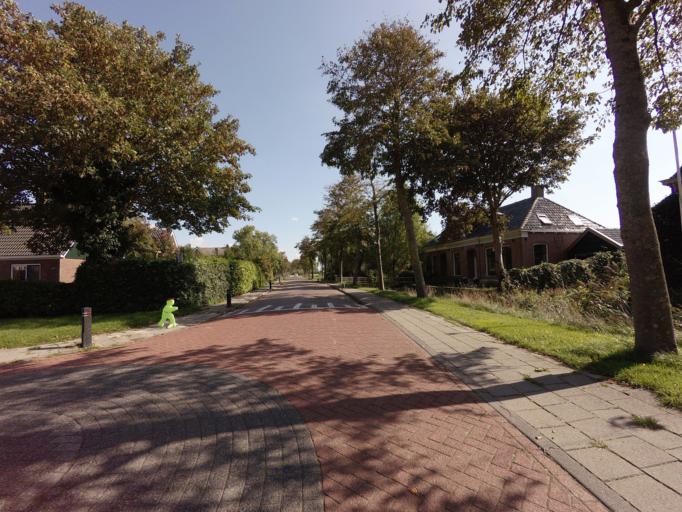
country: NL
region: Friesland
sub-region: Gemeente Littenseradiel
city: Makkum
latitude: 53.0996
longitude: 5.6468
